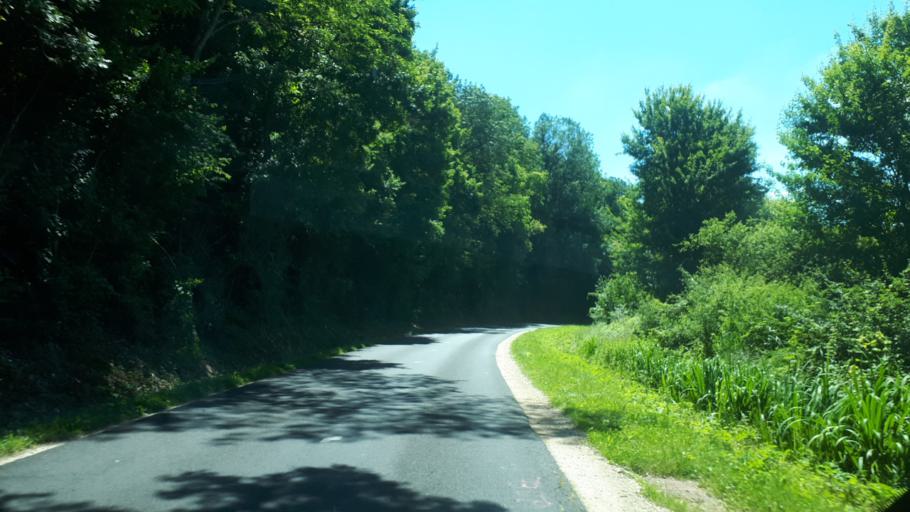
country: FR
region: Centre
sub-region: Departement du Loir-et-Cher
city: Chouzy-sur-Cisse
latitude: 47.5701
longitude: 1.2193
